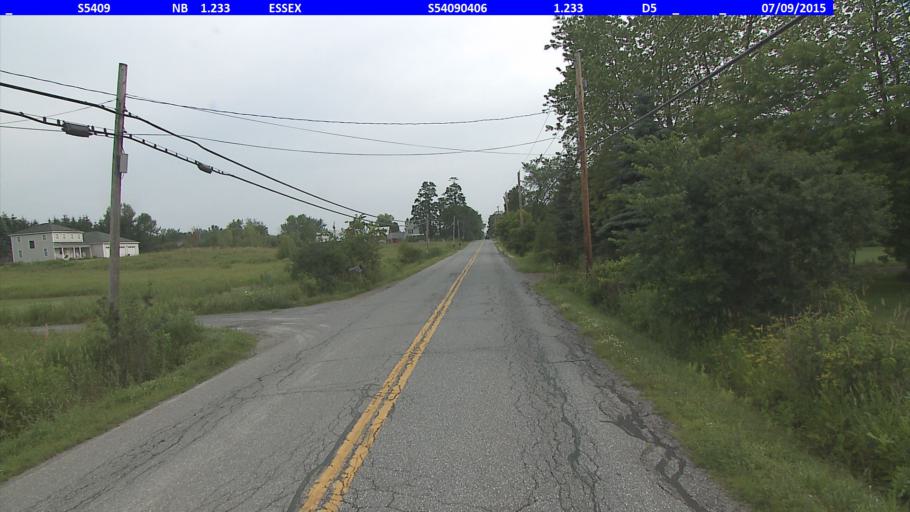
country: US
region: Vermont
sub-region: Chittenden County
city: Essex Junction
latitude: 44.5272
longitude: -73.0778
